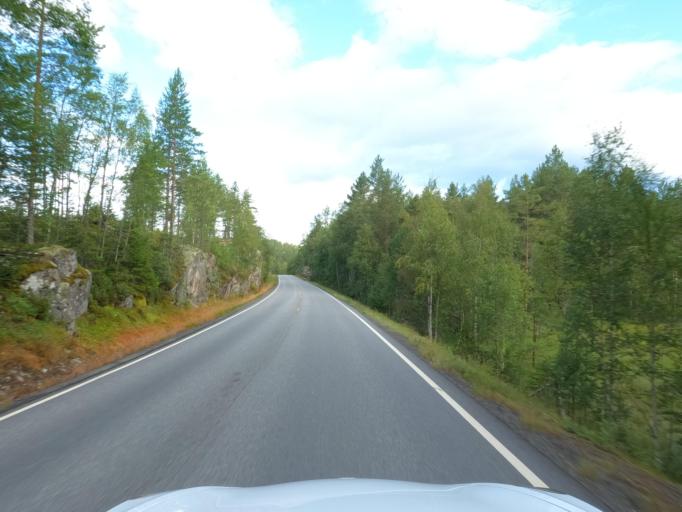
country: NO
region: Telemark
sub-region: Notodden
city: Notodden
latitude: 59.7372
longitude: 9.1553
